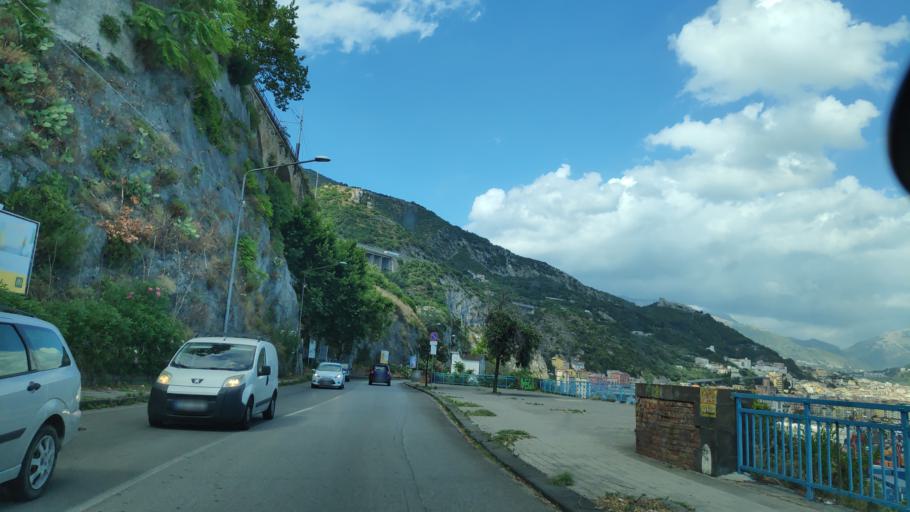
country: IT
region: Campania
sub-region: Provincia di Salerno
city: Vietri sul Mare
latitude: 40.6730
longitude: 14.7353
